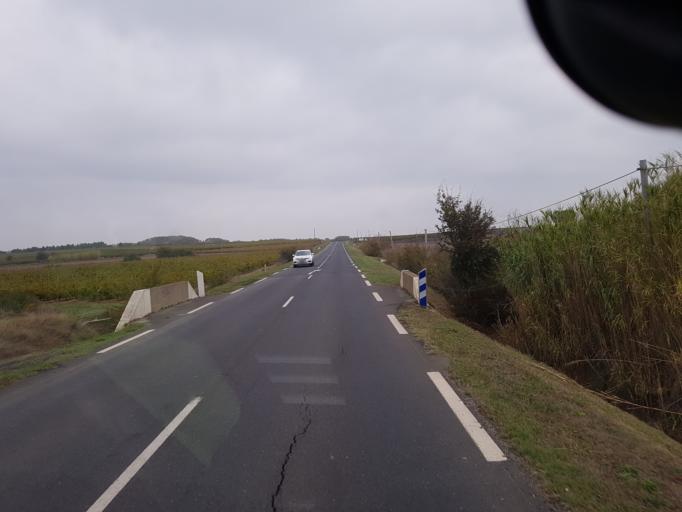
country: FR
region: Languedoc-Roussillon
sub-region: Departement de l'Herault
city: Pinet
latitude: 43.3960
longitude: 3.5385
